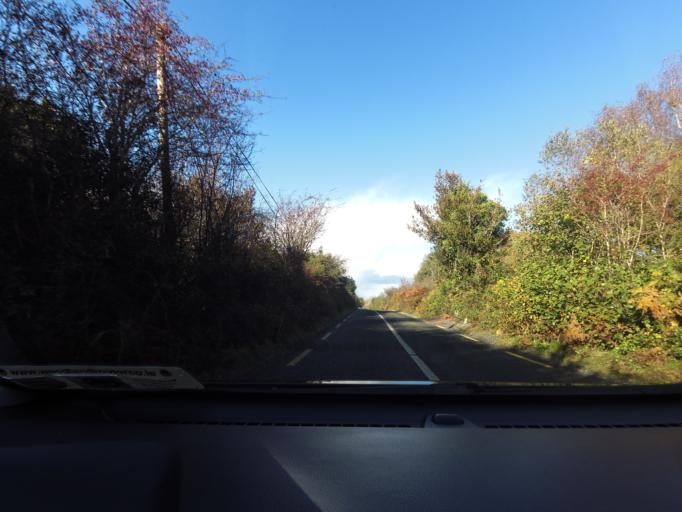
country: IE
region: Connaught
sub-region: Maigh Eo
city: Ballinrobe
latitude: 53.7105
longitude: -9.3091
